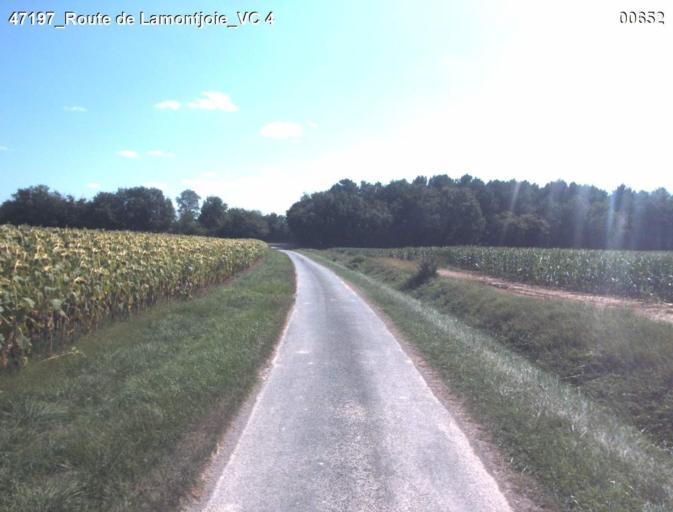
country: FR
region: Aquitaine
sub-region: Departement du Lot-et-Garonne
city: Laplume
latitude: 44.0690
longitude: 0.4926
